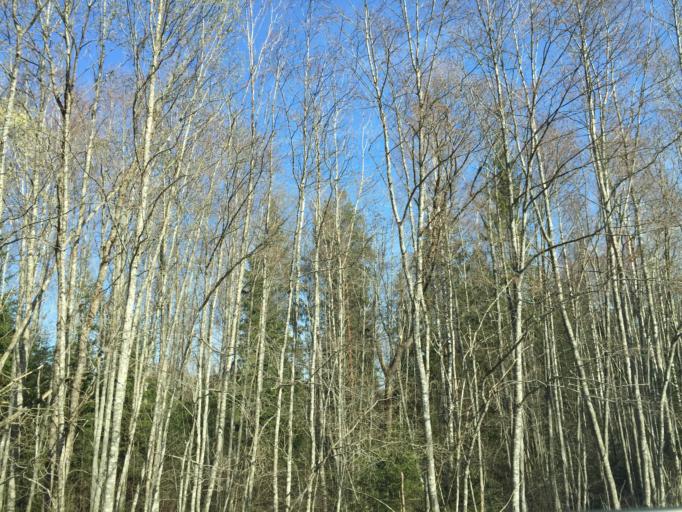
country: EE
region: Vorumaa
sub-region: Antsla vald
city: Vana-Antsla
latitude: 57.9801
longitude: 26.4097
